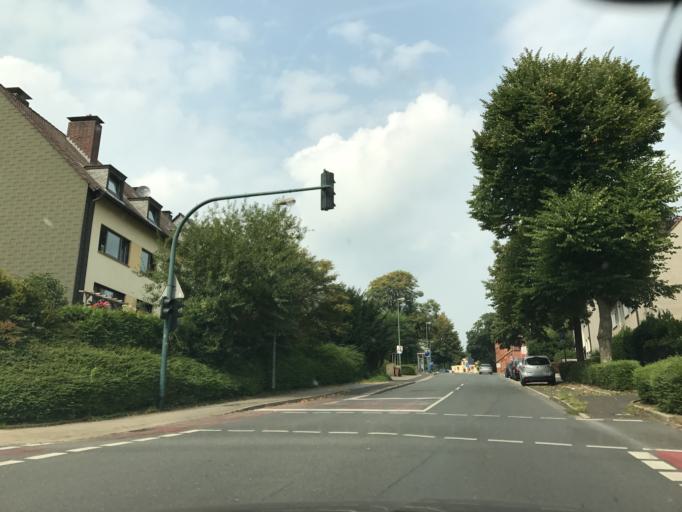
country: DE
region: North Rhine-Westphalia
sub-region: Regierungsbezirk Dusseldorf
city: Oberhausen
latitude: 51.4608
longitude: 6.9433
